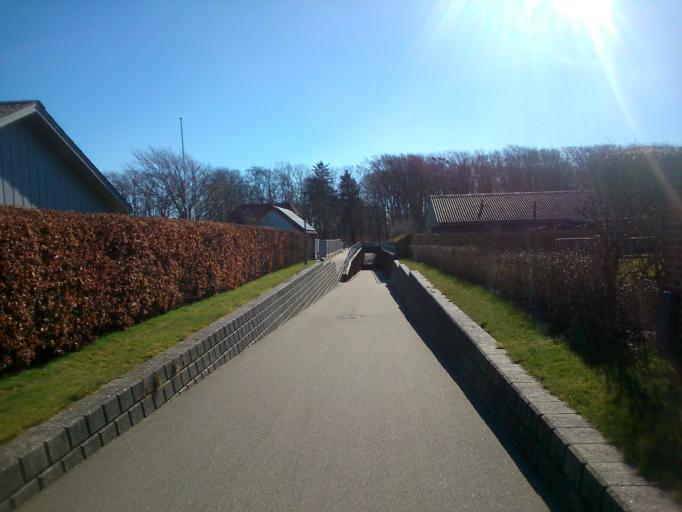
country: DK
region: Central Jutland
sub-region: Ringkobing-Skjern Kommune
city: Ringkobing
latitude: 56.0879
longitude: 8.2631
